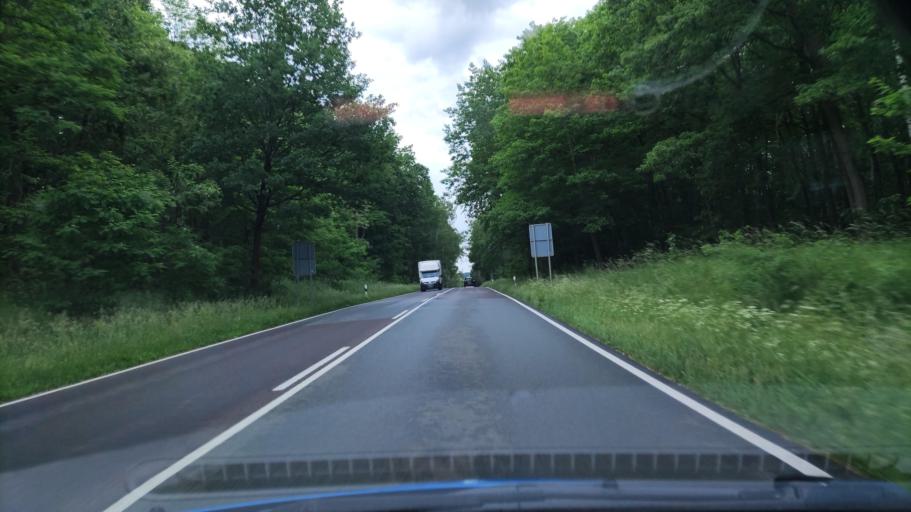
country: DE
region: Saxony-Anhalt
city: Letzlingen
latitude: 52.4058
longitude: 11.4759
